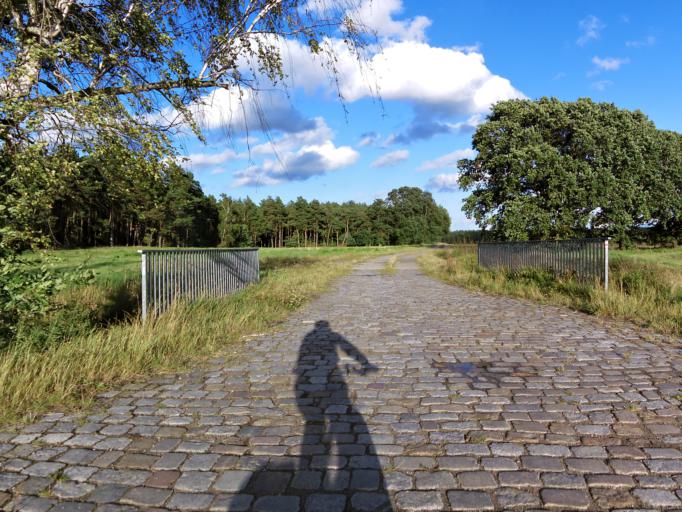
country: DE
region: Saxony-Anhalt
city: Schonebeck
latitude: 52.0709
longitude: 11.7002
